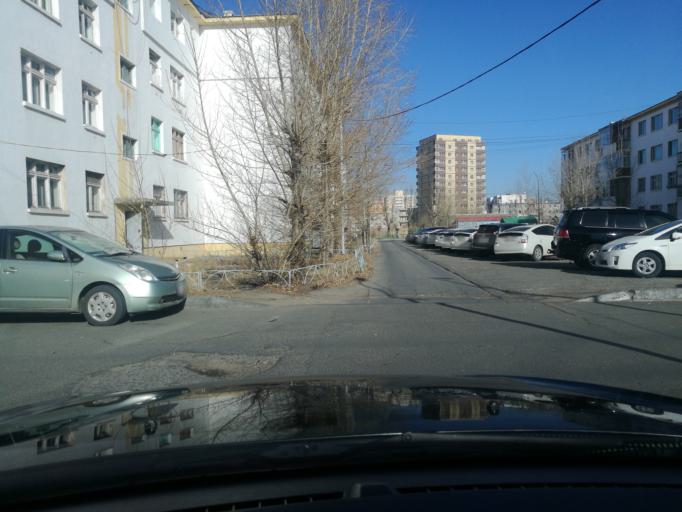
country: MN
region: Ulaanbaatar
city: Ulaanbaatar
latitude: 47.9002
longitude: 106.9044
